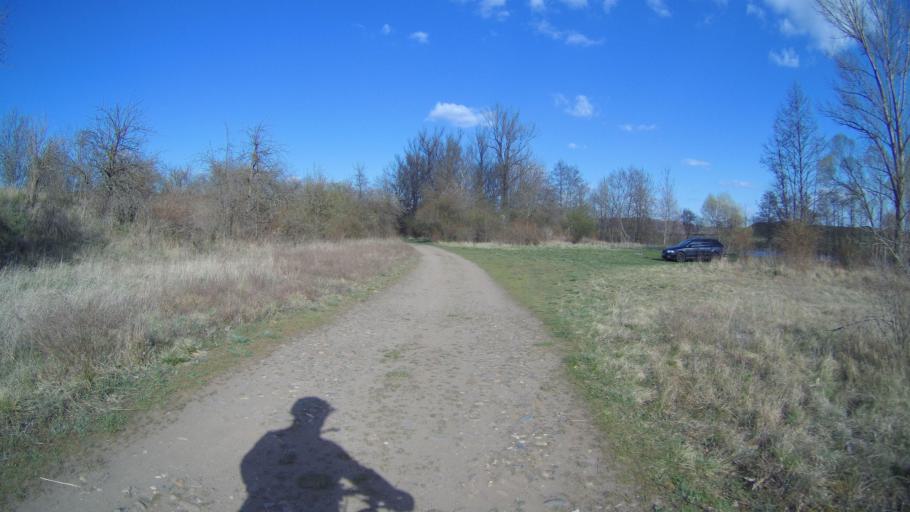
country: CZ
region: Ustecky
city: Zatec
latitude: 50.3544
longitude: 13.4870
